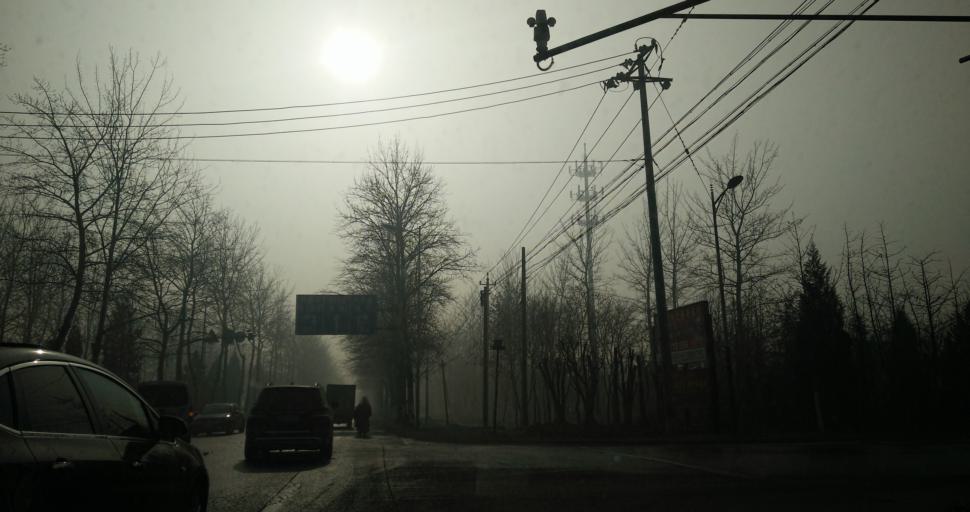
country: CN
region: Beijing
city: Yinghai
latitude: 39.7472
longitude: 116.4472
